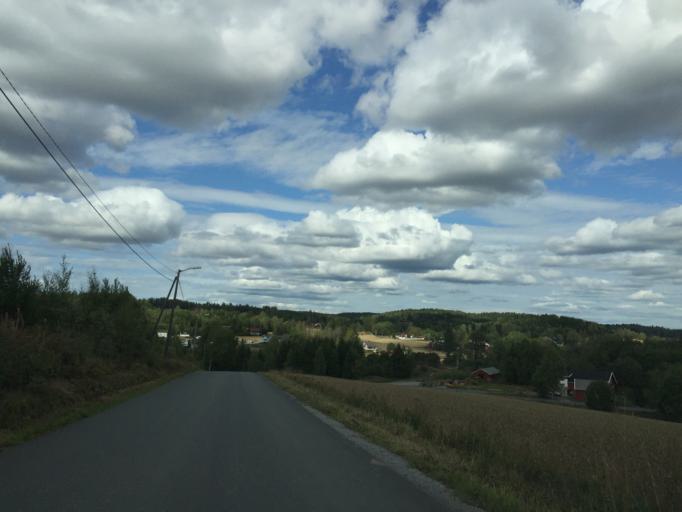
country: NO
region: Ostfold
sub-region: Hobol
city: Elvestad
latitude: 59.6042
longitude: 10.9216
